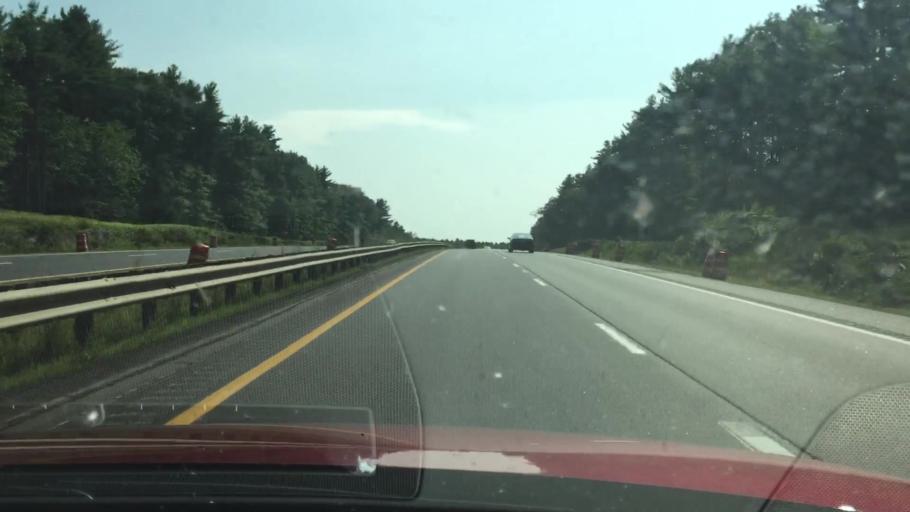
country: US
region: Maine
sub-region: Kennebec County
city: Gardiner
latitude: 44.1753
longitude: -69.8640
